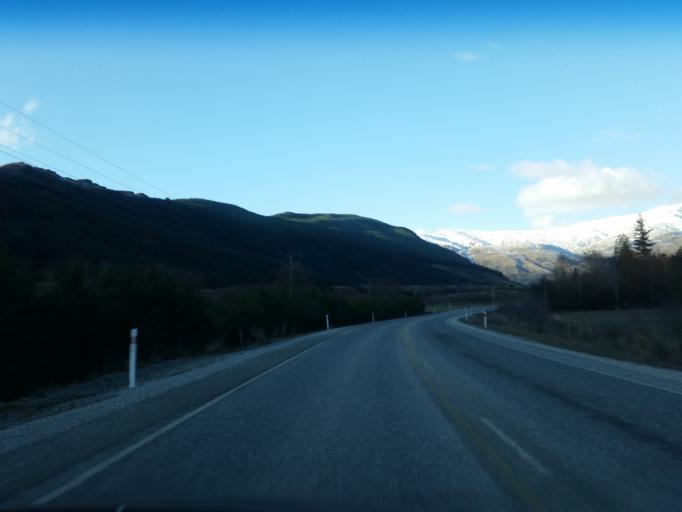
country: NZ
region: Otago
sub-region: Queenstown-Lakes District
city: Arrowtown
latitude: -44.9467
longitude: 168.7675
